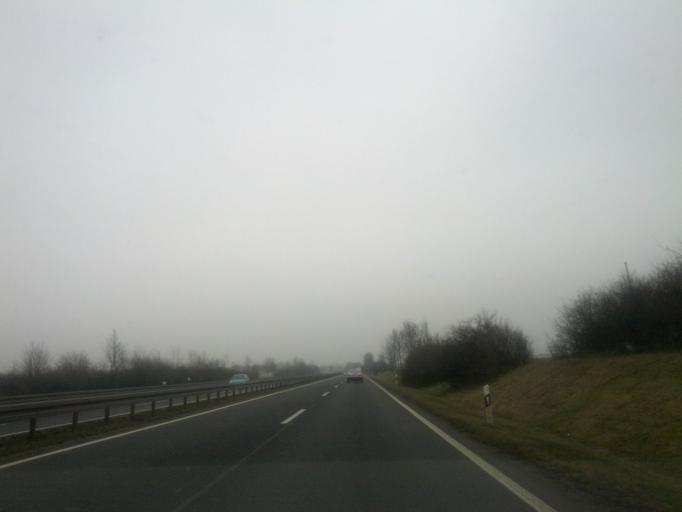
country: DE
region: Thuringia
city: Erfurt
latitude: 50.9692
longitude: 11.0906
